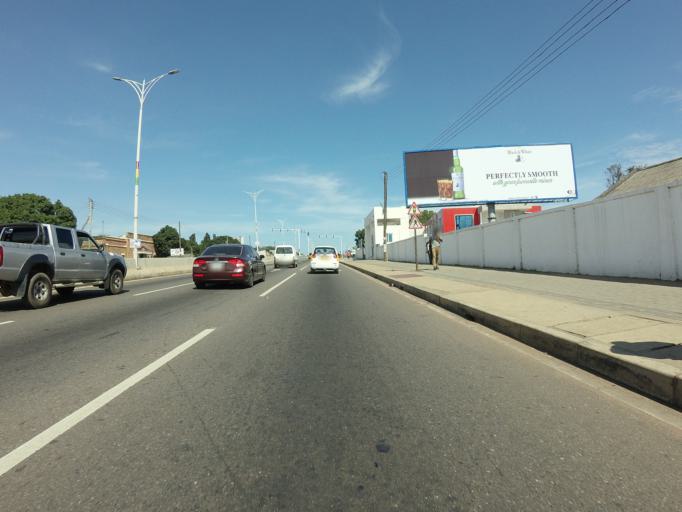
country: GH
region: Greater Accra
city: Accra
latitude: 5.5879
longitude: -0.1772
